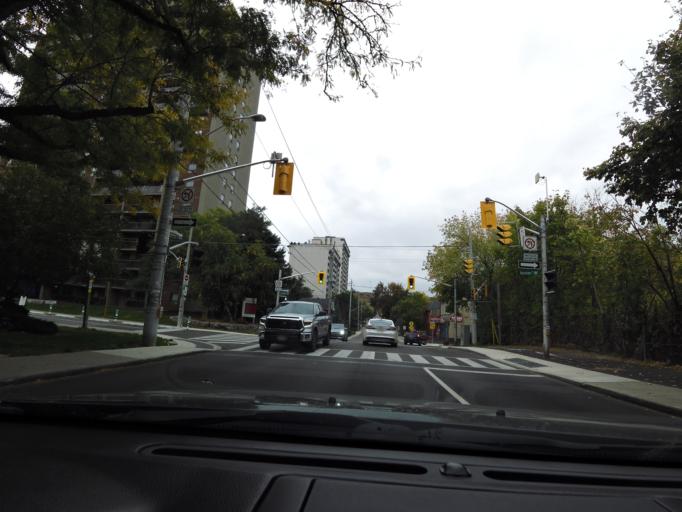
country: CA
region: Ontario
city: Hamilton
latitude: 43.2561
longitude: -79.8800
